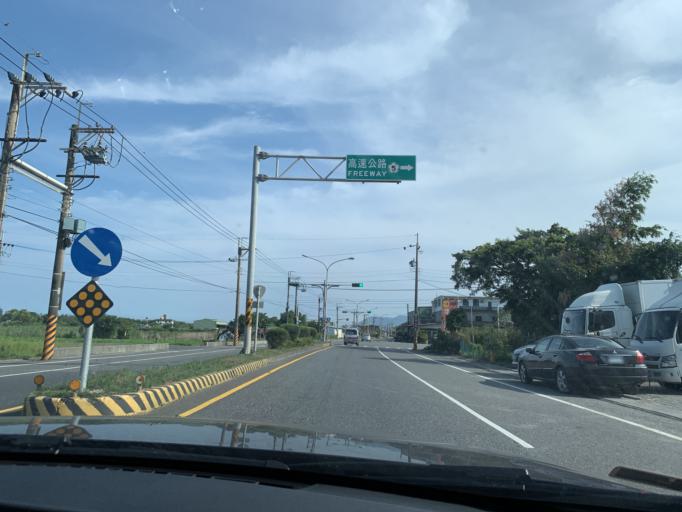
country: TW
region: Taiwan
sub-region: Yilan
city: Yilan
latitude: 24.7364
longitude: 121.8180
